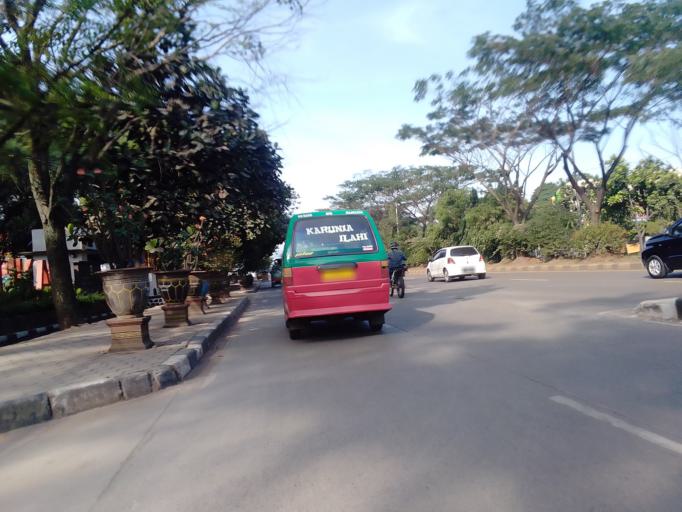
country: ID
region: West Java
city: Cileunyi
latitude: -6.9364
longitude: 107.6993
